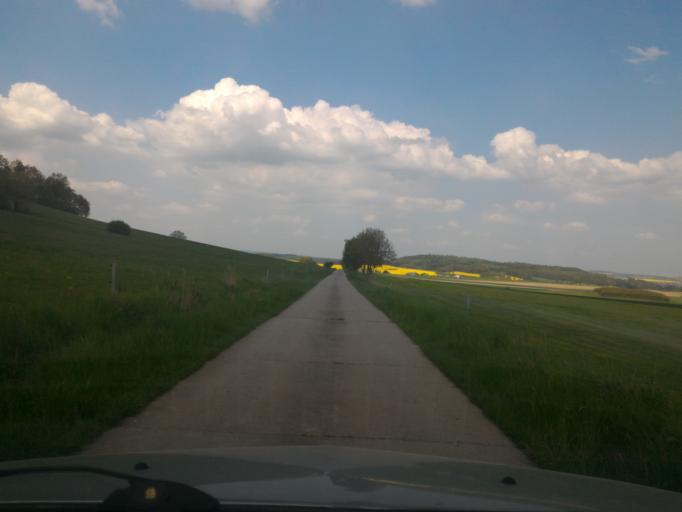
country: DE
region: Saxony
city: Bertsdorf-Hoernitz
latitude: 50.8894
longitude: 14.7111
